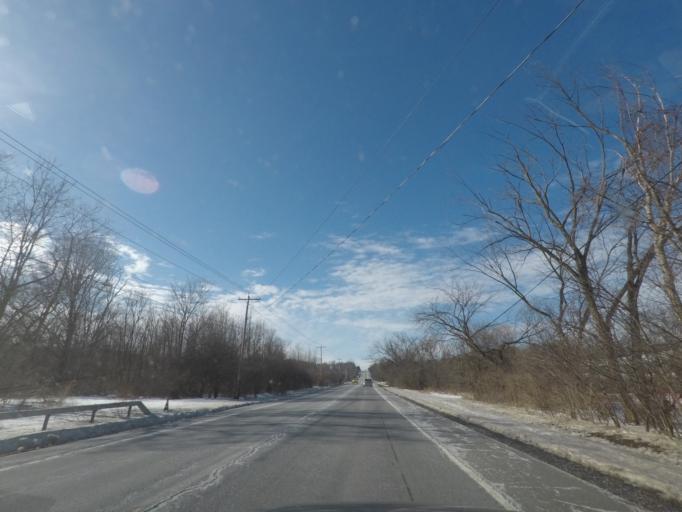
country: US
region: New York
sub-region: Albany County
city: Altamont
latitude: 42.7450
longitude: -74.0315
